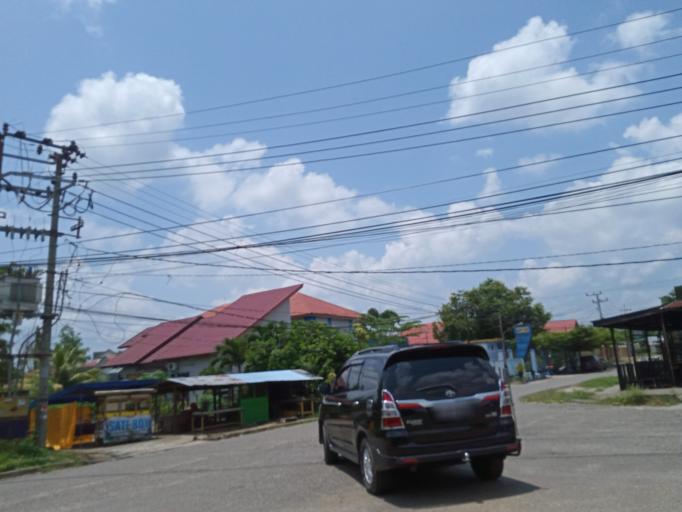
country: ID
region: Jambi
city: Bangko
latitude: -2.0526
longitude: 102.2822
